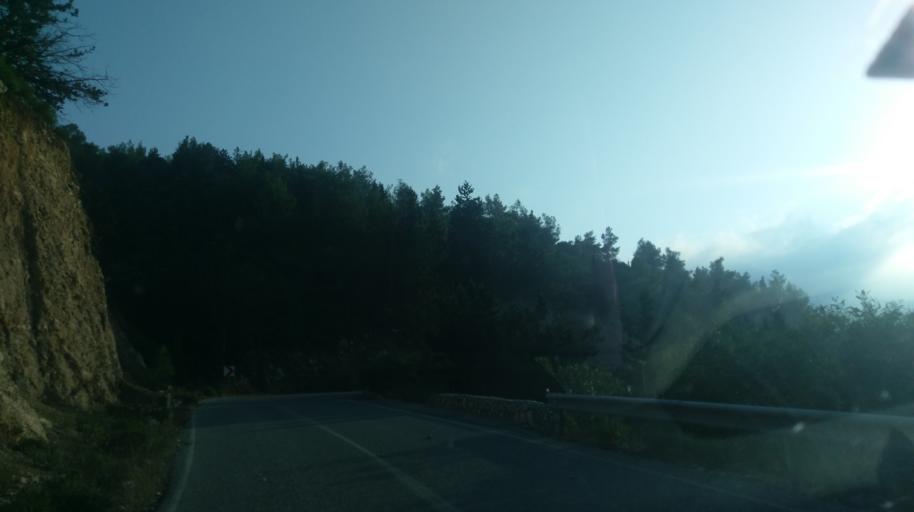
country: CY
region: Ammochostos
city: Trikomo
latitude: 35.3974
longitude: 33.8991
